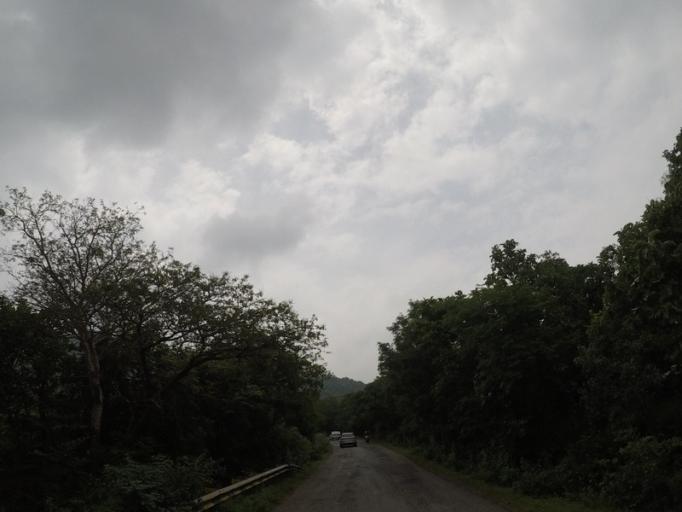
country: IN
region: Karnataka
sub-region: Chikmagalur
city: Birur
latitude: 13.5363
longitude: 75.8209
